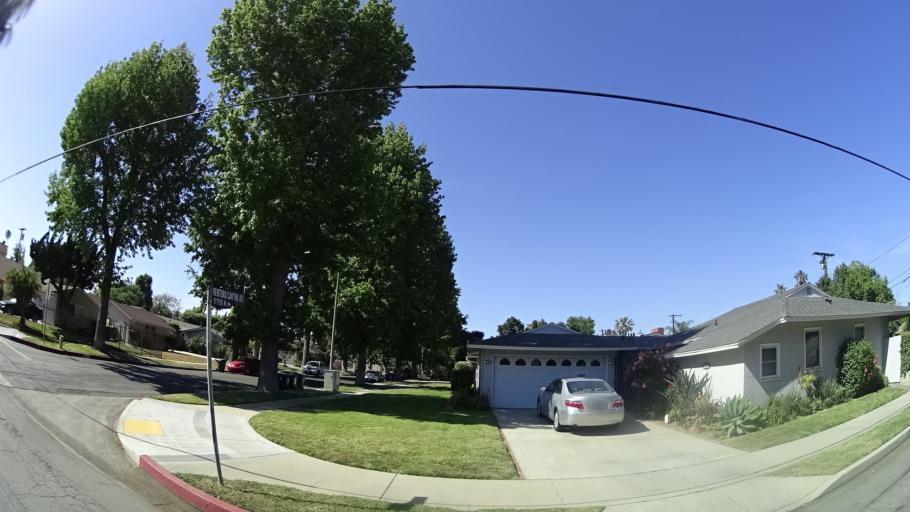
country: US
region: California
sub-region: Los Angeles County
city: Sherman Oaks
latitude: 34.1651
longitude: -118.4290
